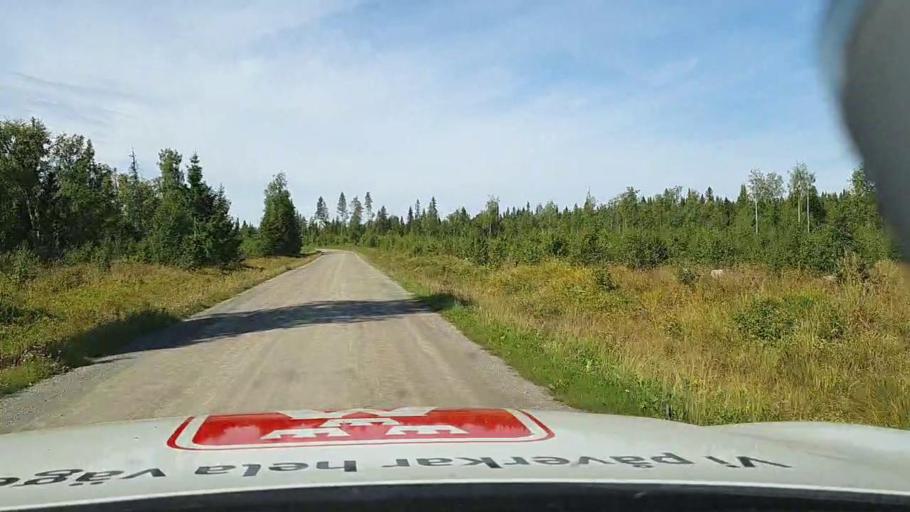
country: SE
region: Jaemtland
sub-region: Stroemsunds Kommun
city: Stroemsund
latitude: 63.7177
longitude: 15.2951
